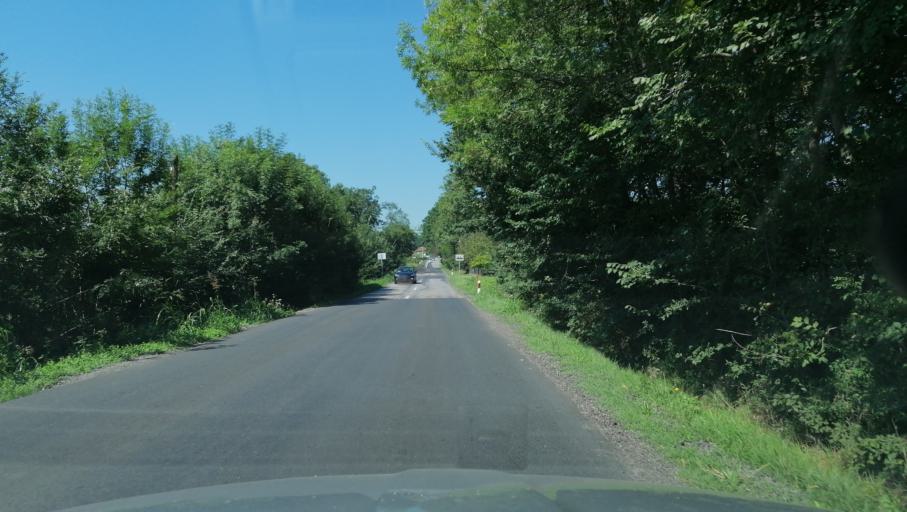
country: RS
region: Central Serbia
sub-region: Raski Okrug
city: Kraljevo
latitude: 43.7171
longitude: 20.8108
